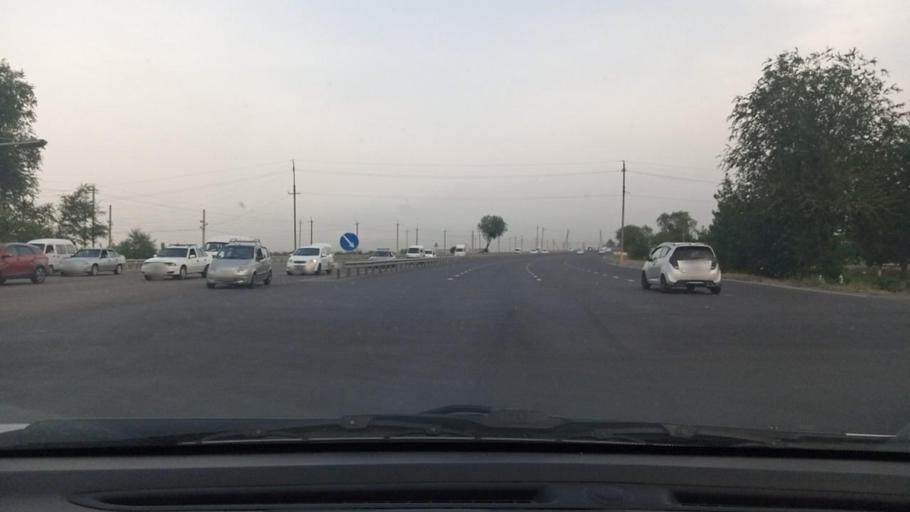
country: UZ
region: Toshkent
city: Ohangaron
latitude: 40.9300
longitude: 69.5953
